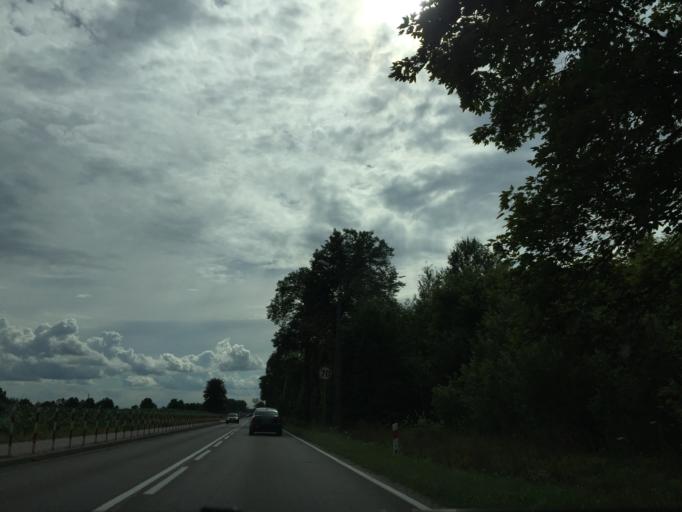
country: PL
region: Lublin Voivodeship
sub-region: Powiat lukowski
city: Lukow
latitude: 51.9428
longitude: 22.4130
